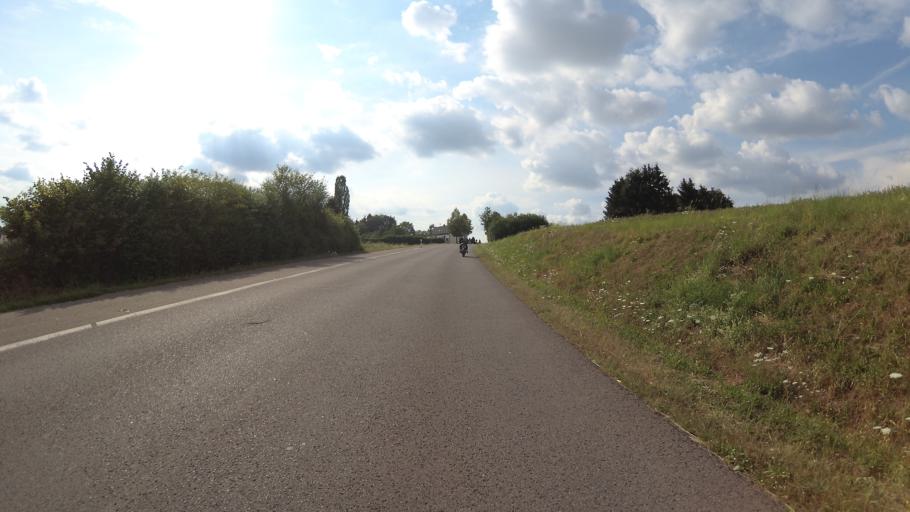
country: DE
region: Saarland
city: Illingen
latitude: 49.3708
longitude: 7.0220
